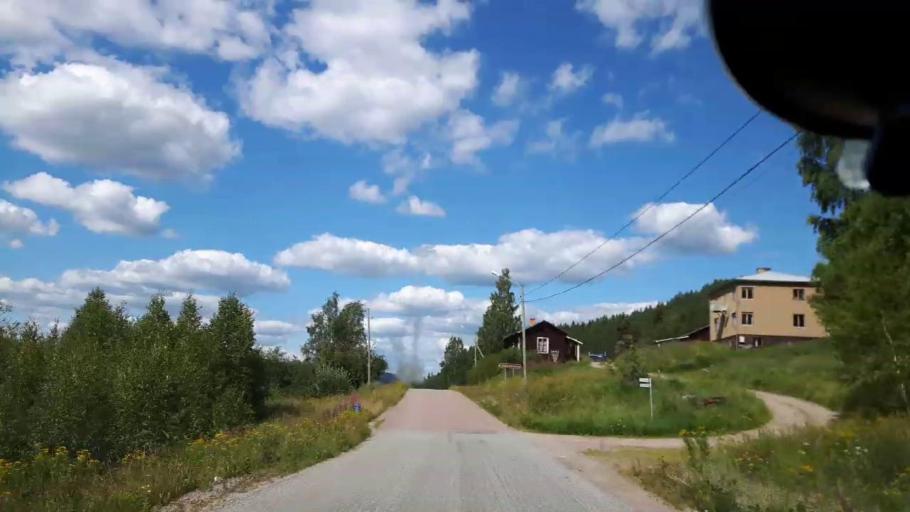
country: SE
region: Jaemtland
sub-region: Ragunda Kommun
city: Hammarstrand
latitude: 62.9535
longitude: 16.6855
